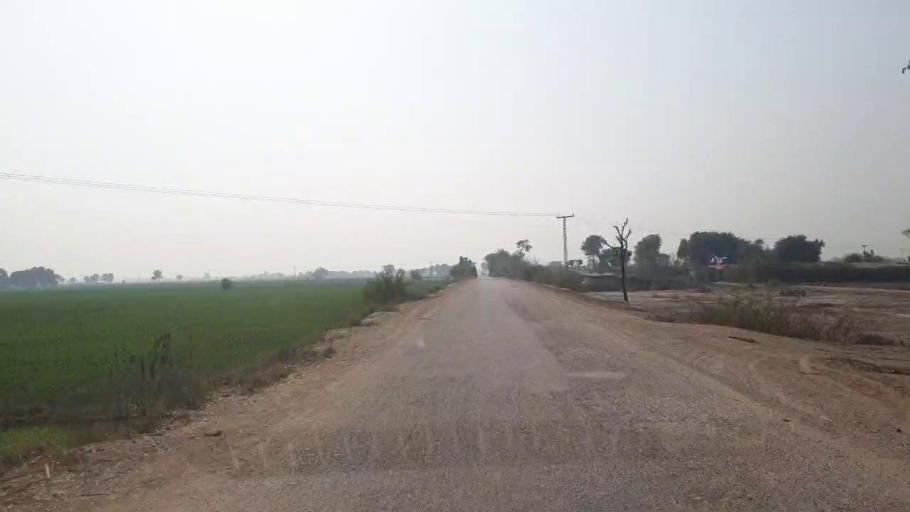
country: PK
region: Sindh
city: Hala
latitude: 25.8795
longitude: 68.4349
